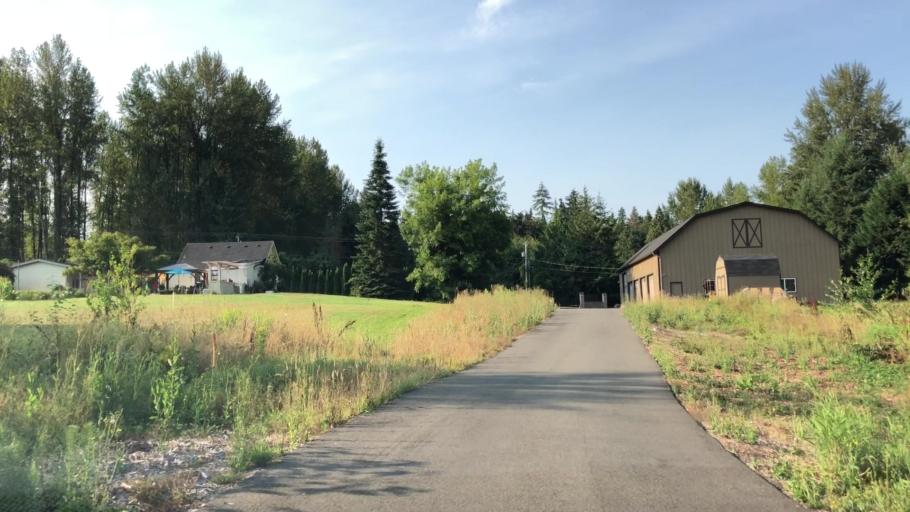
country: US
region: Washington
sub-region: King County
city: Cottage Lake
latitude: 47.7195
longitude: -122.0676
